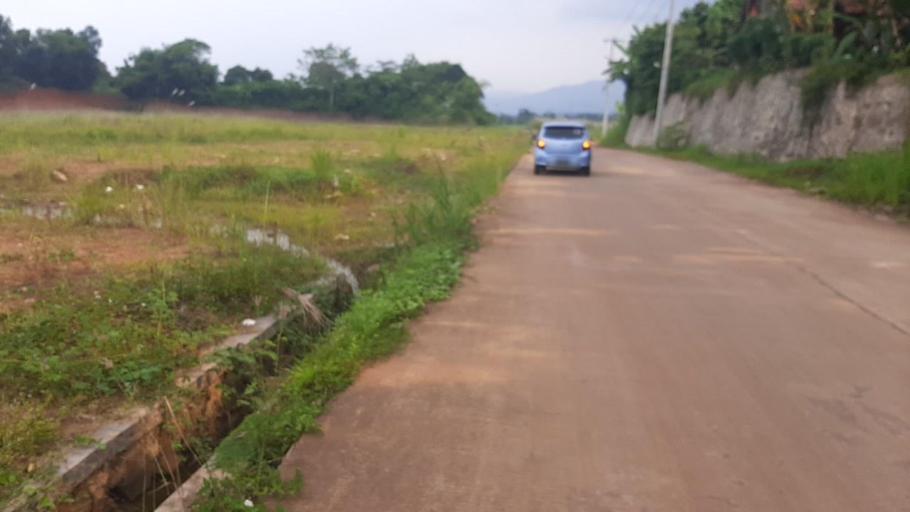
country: ID
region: West Java
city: Cileungsir
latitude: -6.4390
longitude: 107.0239
